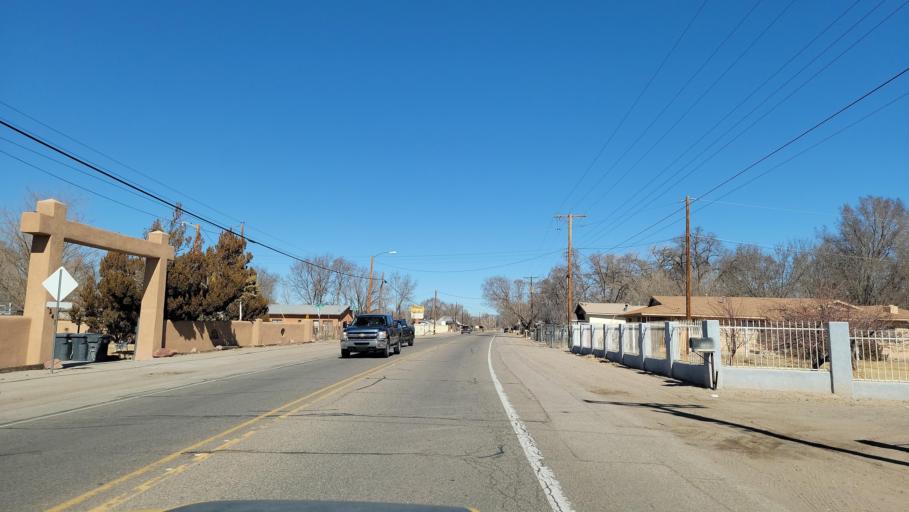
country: US
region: New Mexico
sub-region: Bernalillo County
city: South Valley
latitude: 34.9583
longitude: -106.6959
